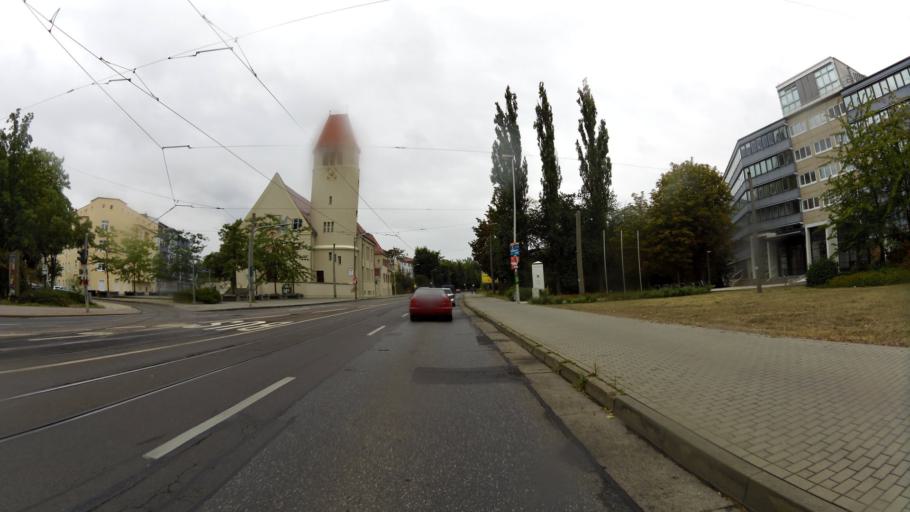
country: DE
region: Brandenburg
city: Cottbus
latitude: 51.7477
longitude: 14.3282
